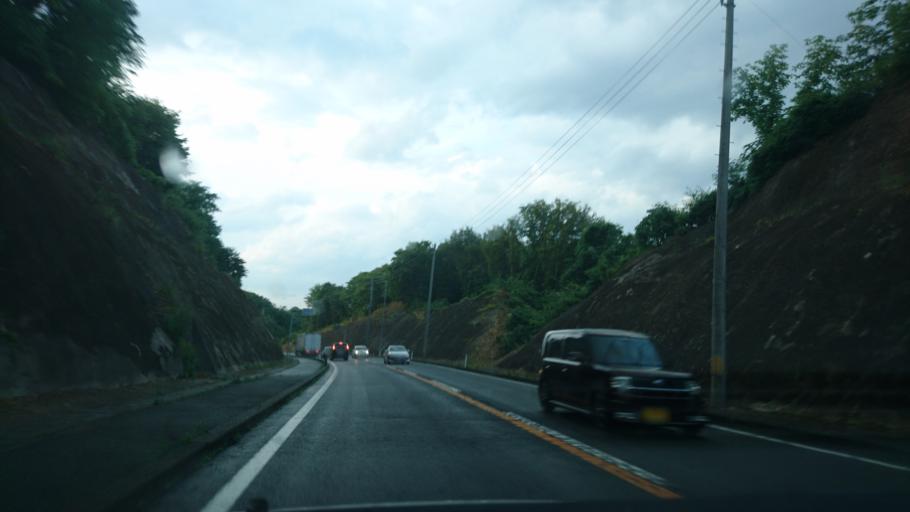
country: JP
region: Iwate
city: Ichinoseki
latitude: 38.9565
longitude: 141.1226
